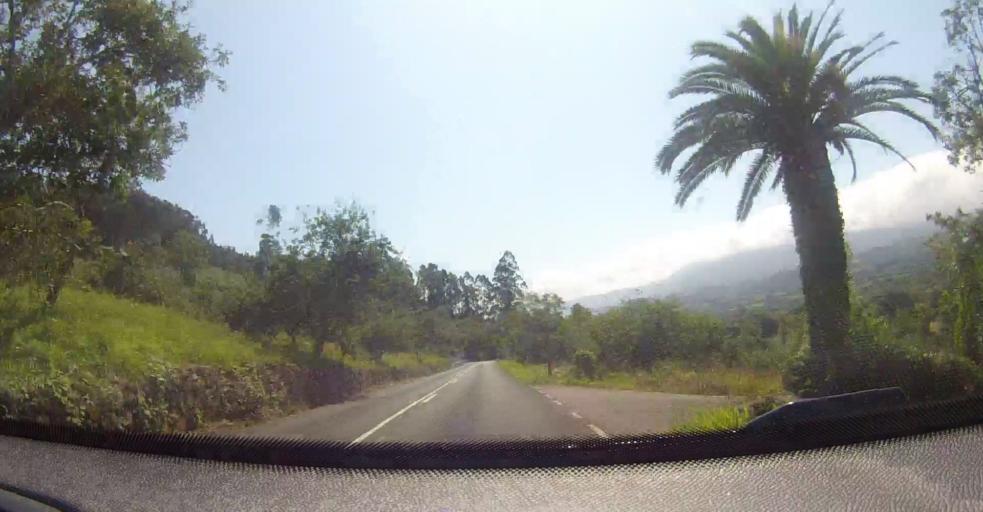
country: ES
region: Asturias
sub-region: Province of Asturias
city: Colunga
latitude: 43.4909
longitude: -5.3138
